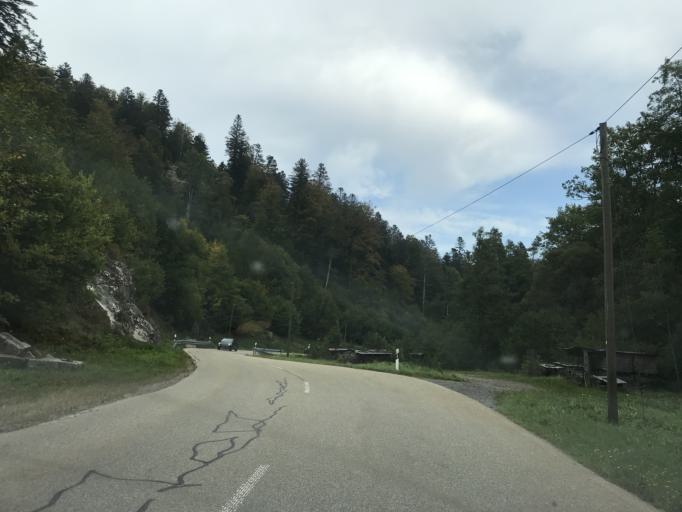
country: DE
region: Baden-Wuerttemberg
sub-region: Freiburg Region
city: Herrischried
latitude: 47.6934
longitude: 7.9706
